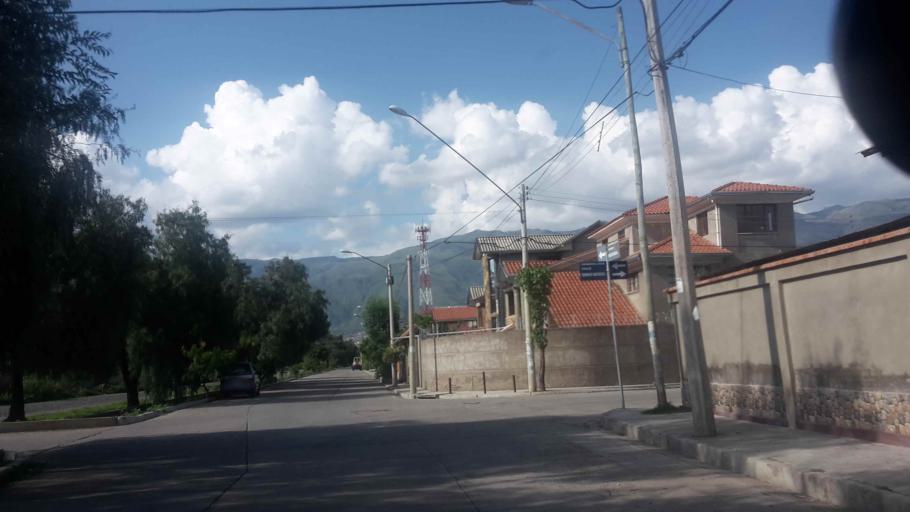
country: BO
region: Cochabamba
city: Cochabamba
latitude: -17.3844
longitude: -66.1963
